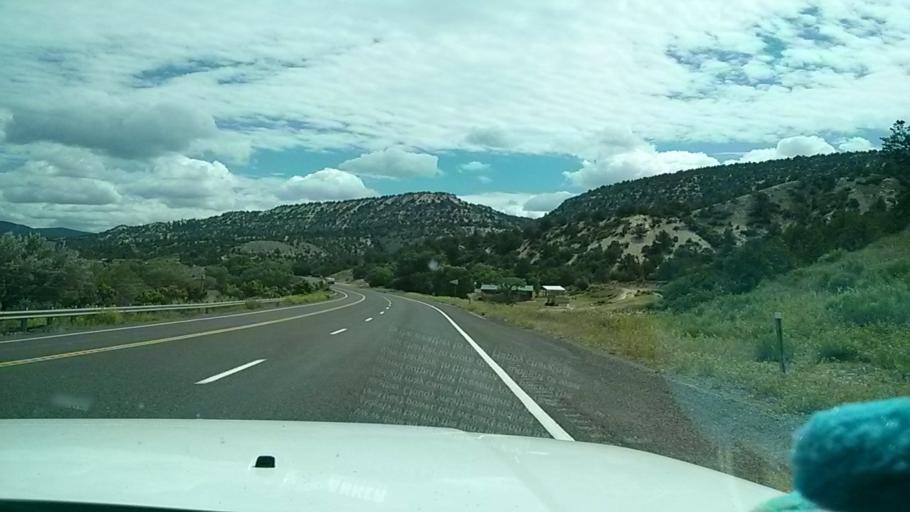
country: US
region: Utah
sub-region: Kane County
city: Kanab
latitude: 37.2996
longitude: -112.6093
